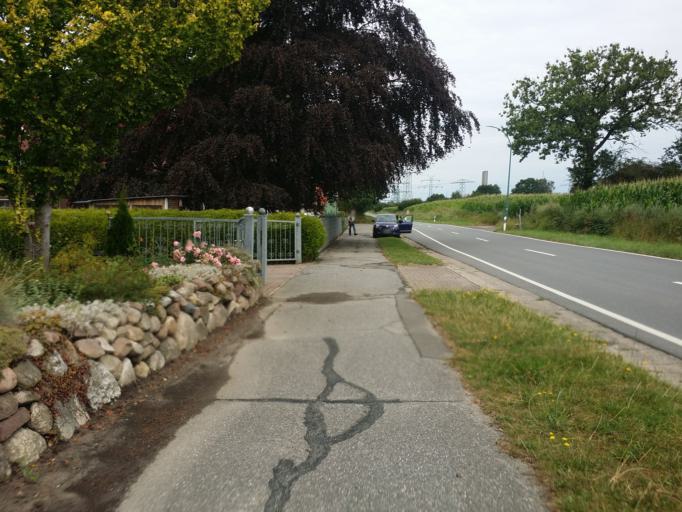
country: DE
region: Schleswig-Holstein
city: Oldendorf
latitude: 53.9609
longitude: 9.4493
